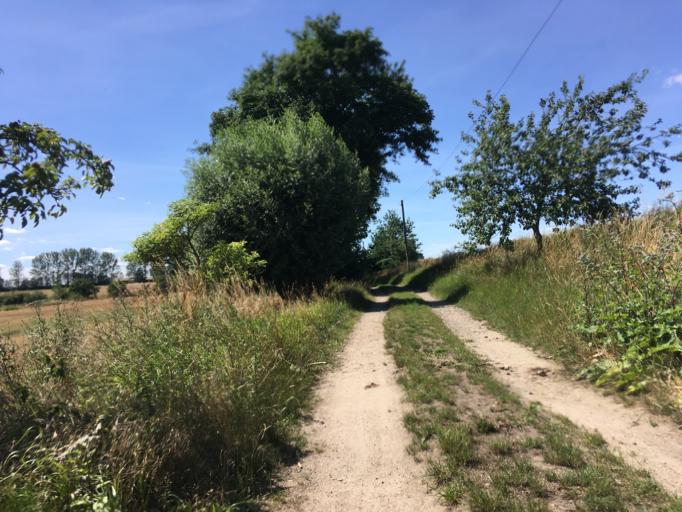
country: DE
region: Brandenburg
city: Brussow
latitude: 53.3254
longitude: 14.0882
